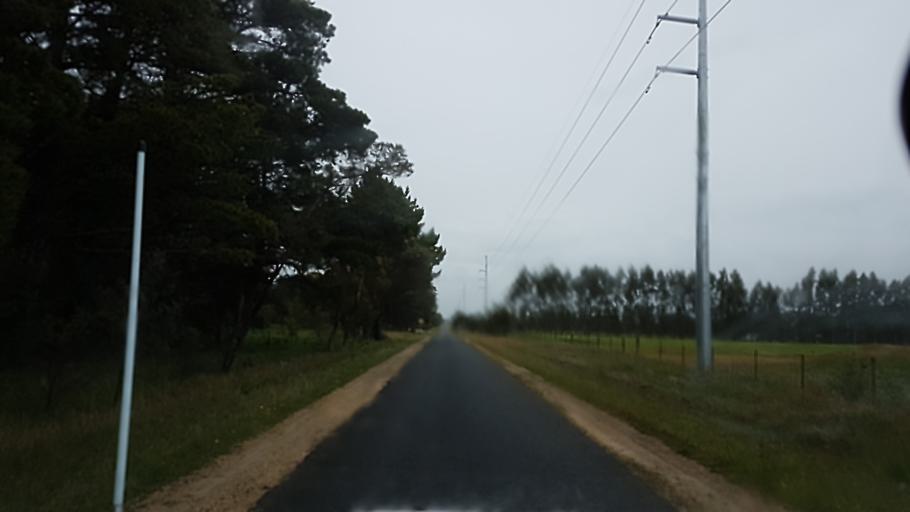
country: AU
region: Victoria
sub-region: Ballarat North
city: Mount Clear
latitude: -37.7817
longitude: 143.9803
